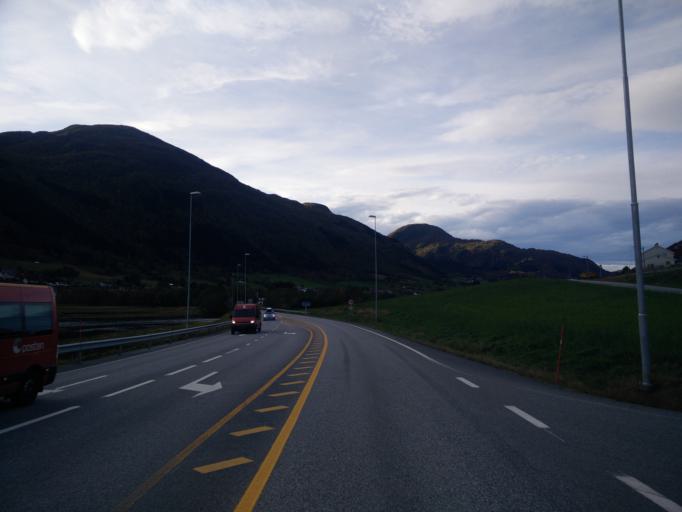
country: NO
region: More og Romsdal
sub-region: Gjemnes
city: Batnfjordsora
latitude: 62.9010
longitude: 7.6768
